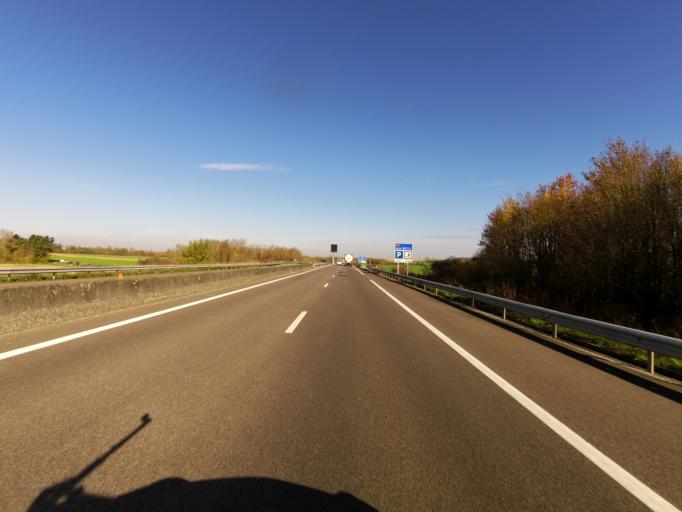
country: FR
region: Champagne-Ardenne
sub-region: Departement de la Marne
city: Fagnieres
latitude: 48.9994
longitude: 4.2977
